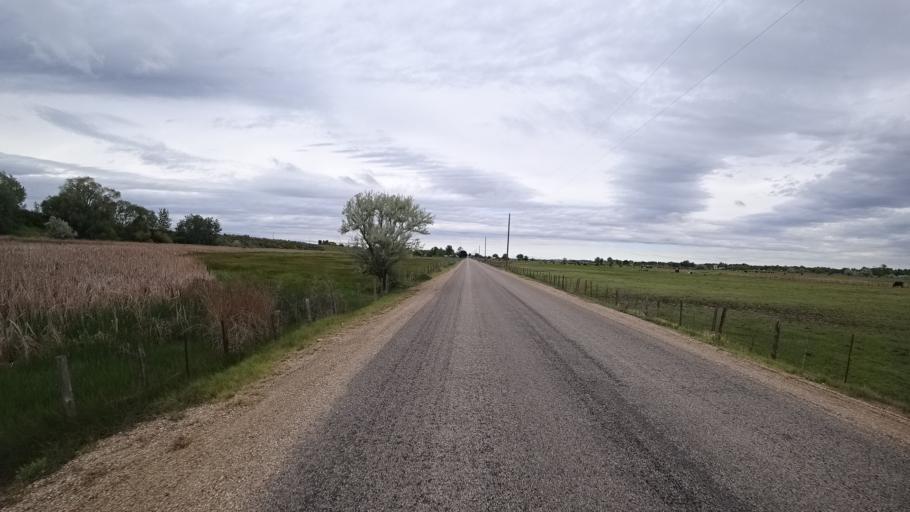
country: US
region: Idaho
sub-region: Ada County
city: Star
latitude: 43.6703
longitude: -116.4815
